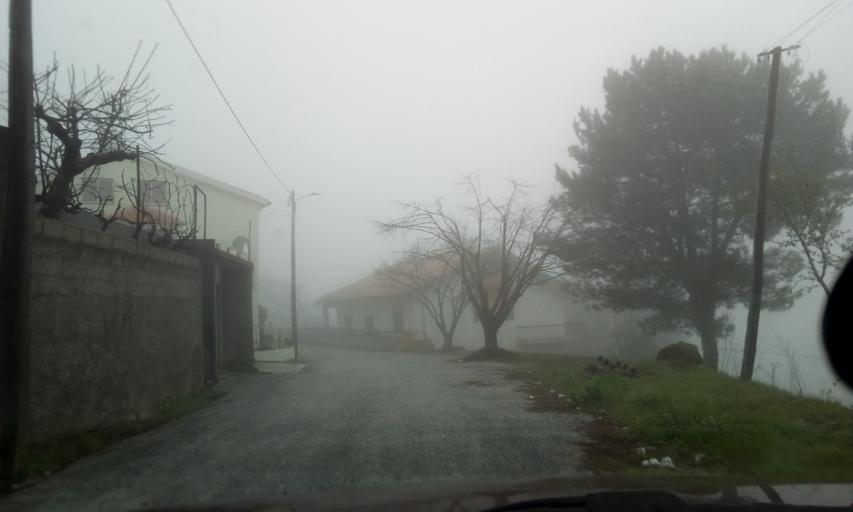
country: PT
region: Guarda
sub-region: Fornos de Algodres
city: Fornos de Algodres
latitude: 40.6272
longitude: -7.5403
